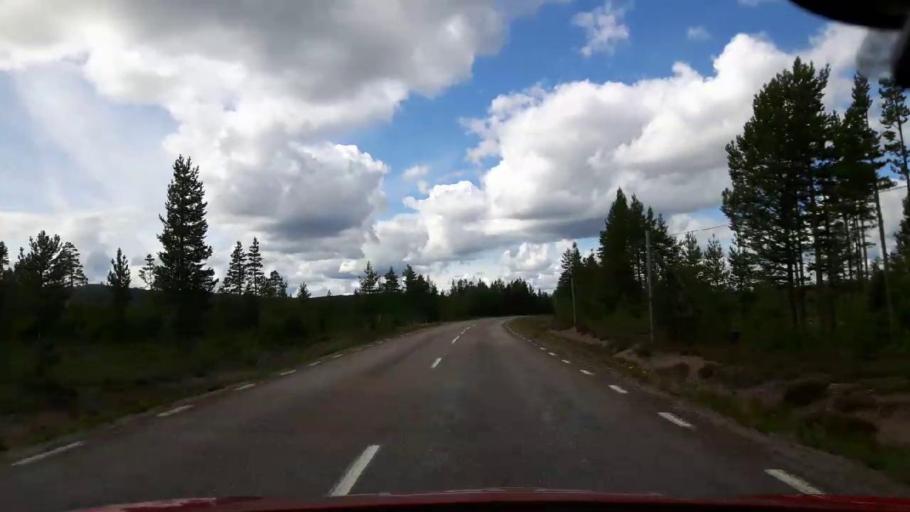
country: SE
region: Jaemtland
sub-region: Harjedalens Kommun
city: Sveg
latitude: 61.8411
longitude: 14.0294
